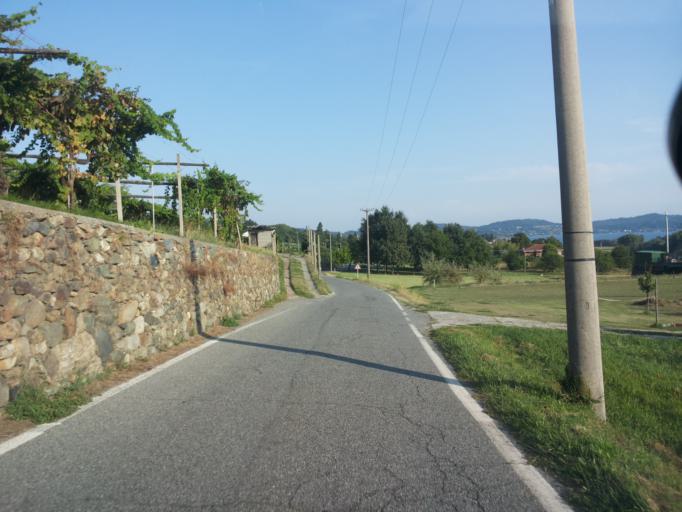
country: IT
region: Piedmont
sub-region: Provincia di Torino
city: Piverone
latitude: 45.4426
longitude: 8.0159
